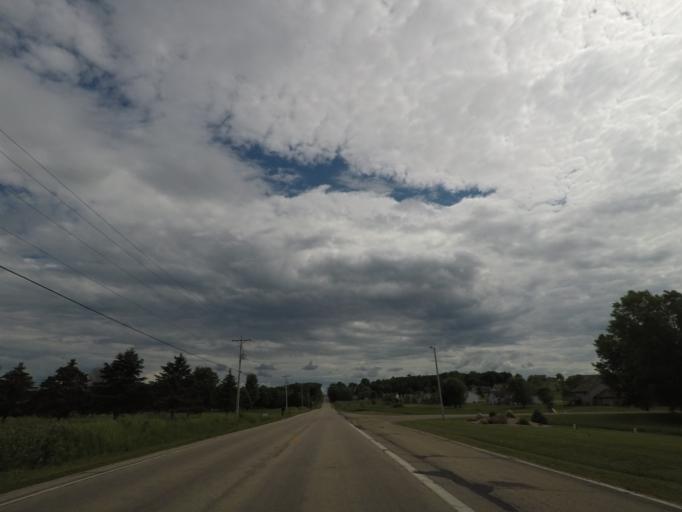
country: US
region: Wisconsin
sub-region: Dane County
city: Belleville
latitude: 42.8404
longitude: -89.5254
